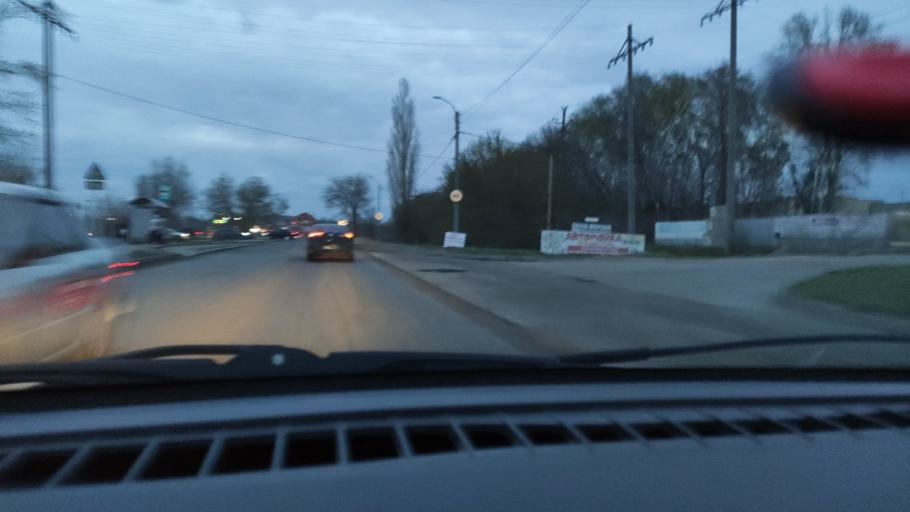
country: RU
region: Orenburg
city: Tatarskaya Kargala
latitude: 51.8667
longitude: 55.1409
